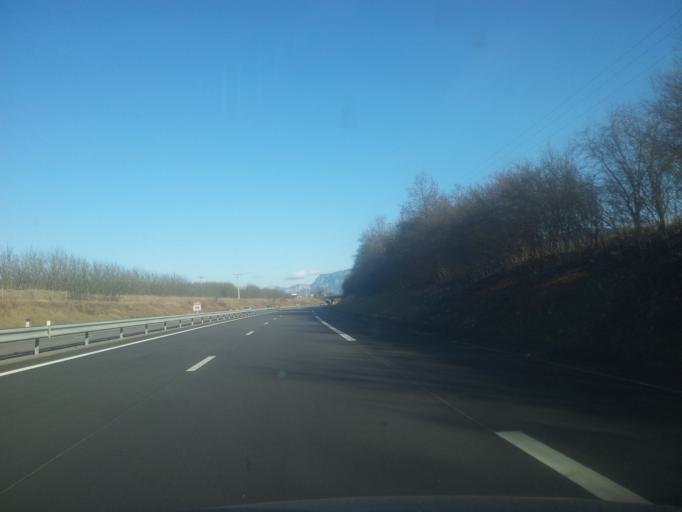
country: FR
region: Rhone-Alpes
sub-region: Departement de l'Isere
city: Chatte
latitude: 45.1204
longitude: 5.2719
